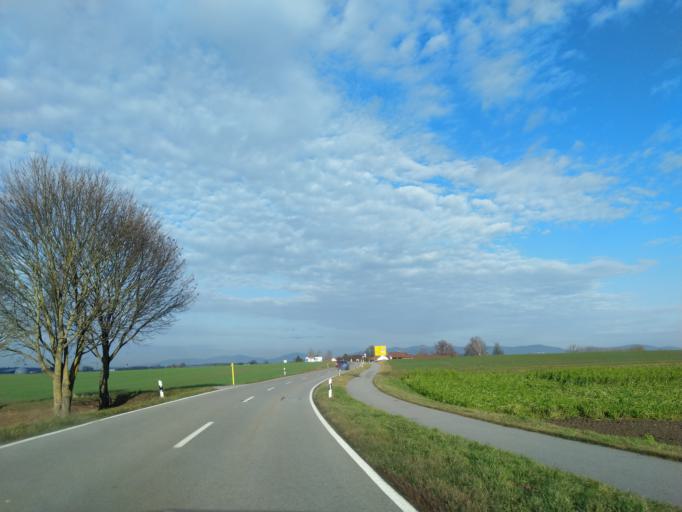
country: DE
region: Bavaria
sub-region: Lower Bavaria
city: Osterhofen
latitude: 48.7141
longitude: 13.0152
